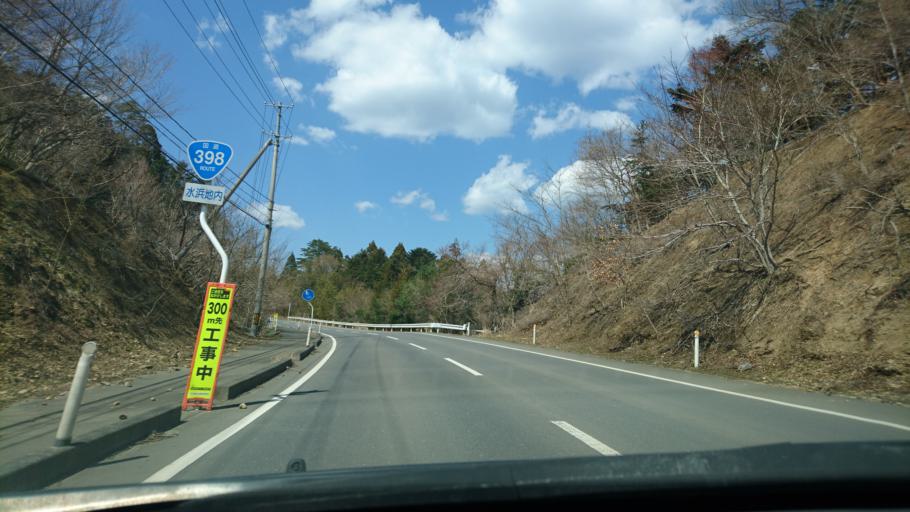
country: JP
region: Miyagi
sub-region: Oshika Gun
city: Onagawa Cho
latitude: 38.5068
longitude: 141.4868
